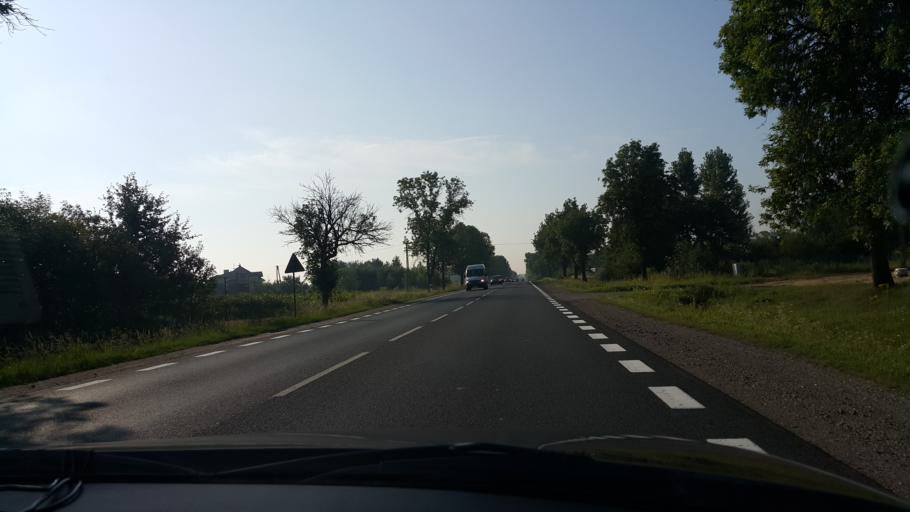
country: PL
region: Masovian Voivodeship
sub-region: Powiat radomski
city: Jedlnia-Letnisko
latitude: 51.3971
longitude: 21.2620
